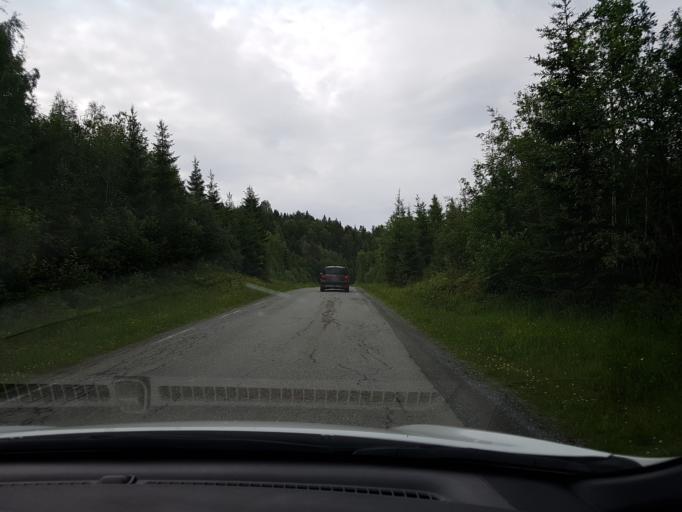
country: NO
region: Nord-Trondelag
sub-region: Frosta
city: Frosta
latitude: 63.6205
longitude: 10.7602
